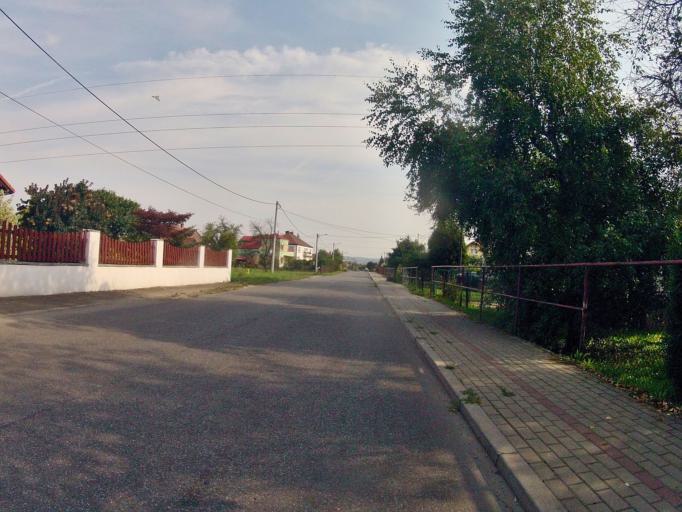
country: PL
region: Subcarpathian Voivodeship
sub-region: Powiat jasielski
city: Jaslo
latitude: 49.7319
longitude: 21.4502
